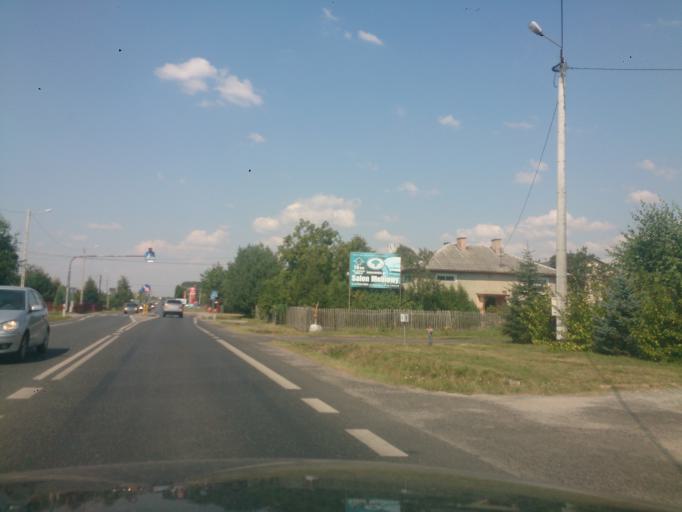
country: PL
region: Subcarpathian Voivodeship
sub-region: Powiat kolbuszowski
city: Kolbuszowa
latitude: 50.2564
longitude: 21.7683
